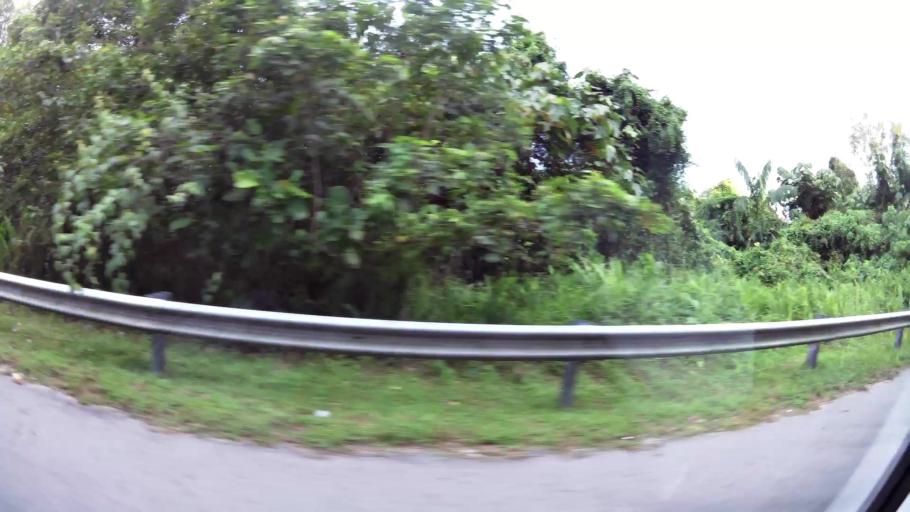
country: BN
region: Brunei and Muara
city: Bandar Seri Begawan
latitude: 4.9077
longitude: 114.9967
